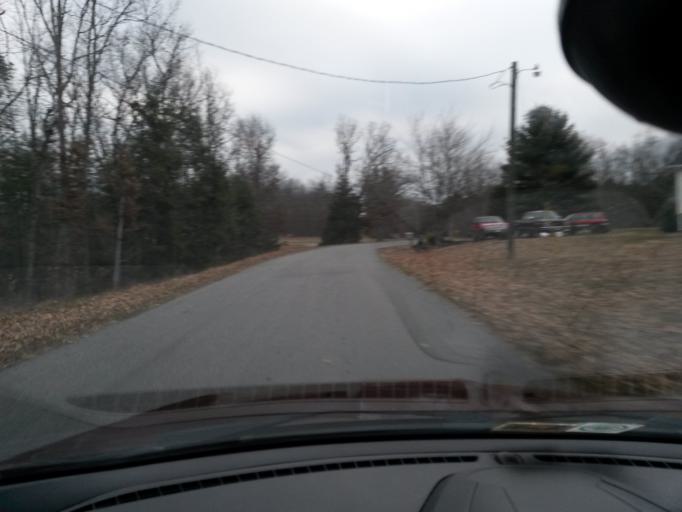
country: US
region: Virginia
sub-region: Bath County
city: Warm Springs
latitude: 37.9899
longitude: -79.6010
